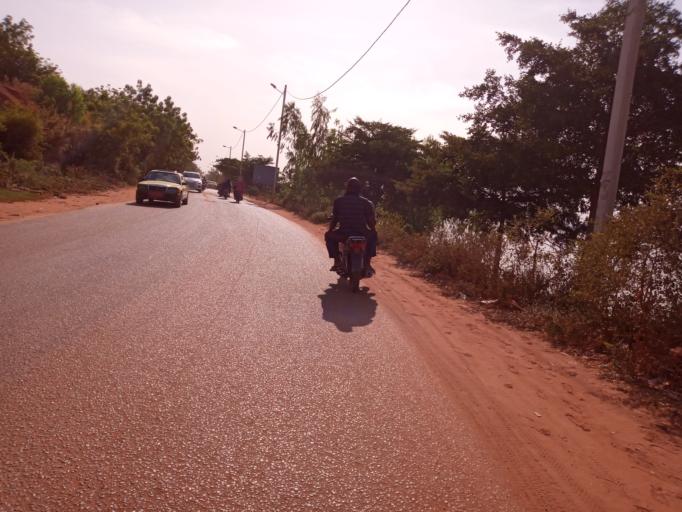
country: ML
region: Bamako
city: Bamako
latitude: 12.6297
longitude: -7.9522
